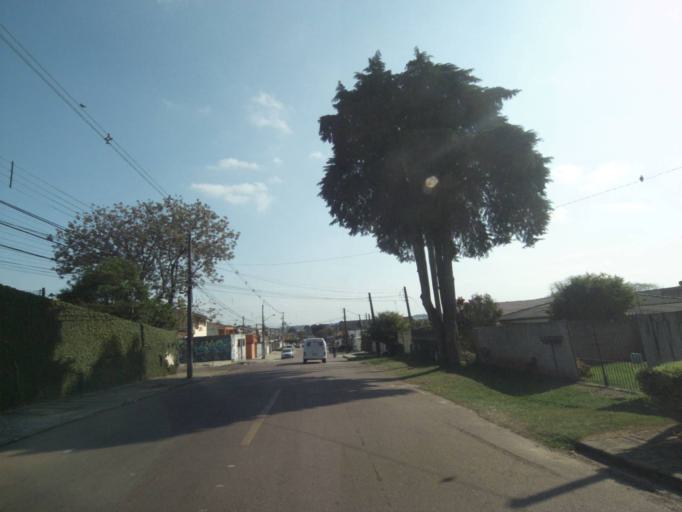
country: BR
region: Parana
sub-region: Curitiba
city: Curitiba
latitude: -25.4881
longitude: -49.3301
